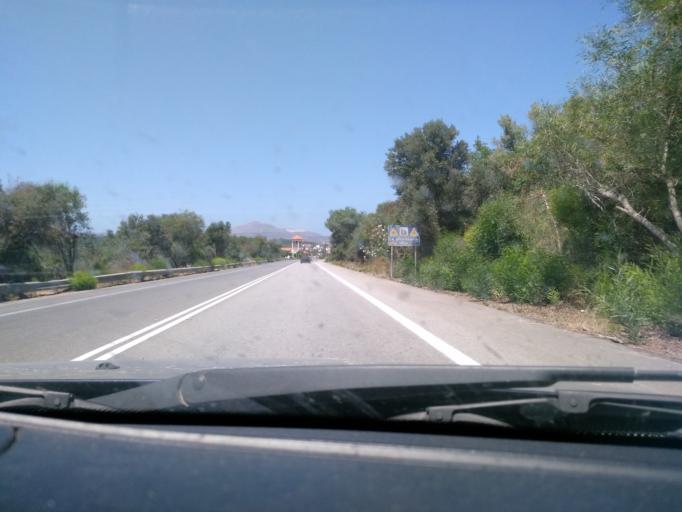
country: GR
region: Crete
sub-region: Nomos Chanias
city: Kalivai
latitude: 35.4357
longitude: 24.1663
